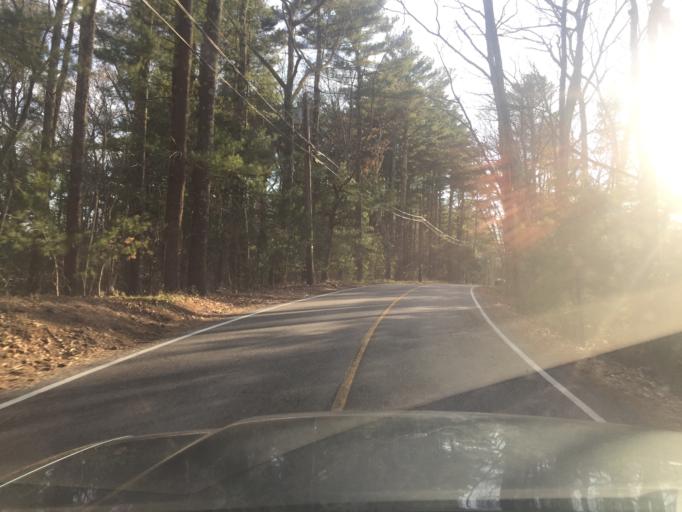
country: US
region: Massachusetts
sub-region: Middlesex County
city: Sherborn
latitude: 42.2316
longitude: -71.3359
